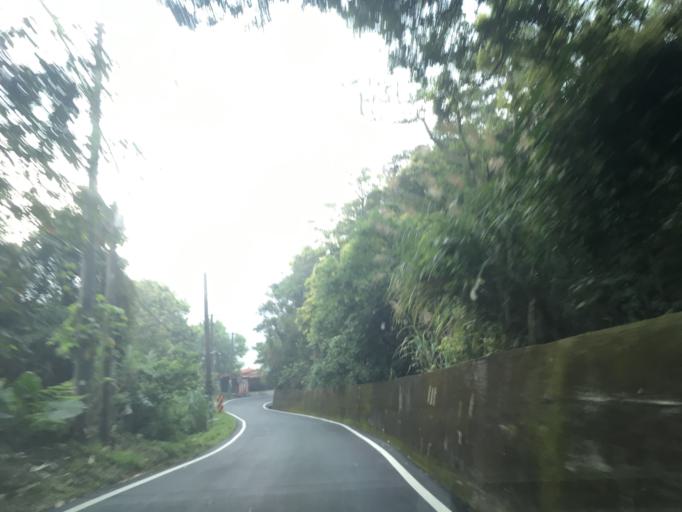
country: TW
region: Taiwan
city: Daxi
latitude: 24.8813
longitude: 121.3059
